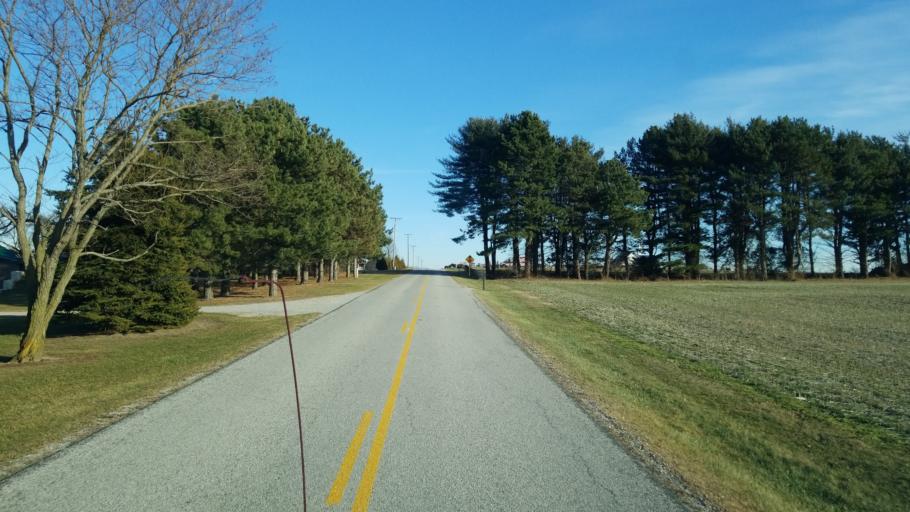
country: US
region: Ohio
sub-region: Sandusky County
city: Clyde
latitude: 41.2561
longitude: -82.9837
